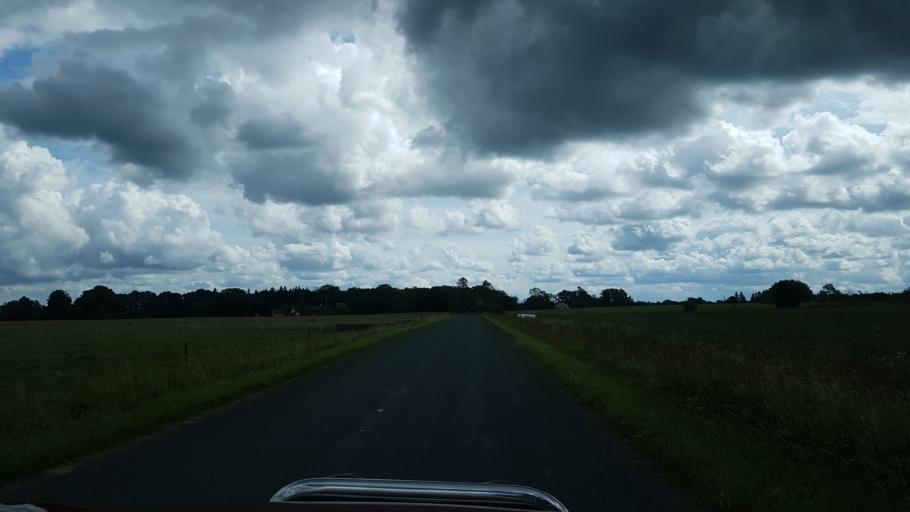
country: EE
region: Laeaene
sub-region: Lihula vald
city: Lihula
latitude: 58.7097
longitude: 24.0153
